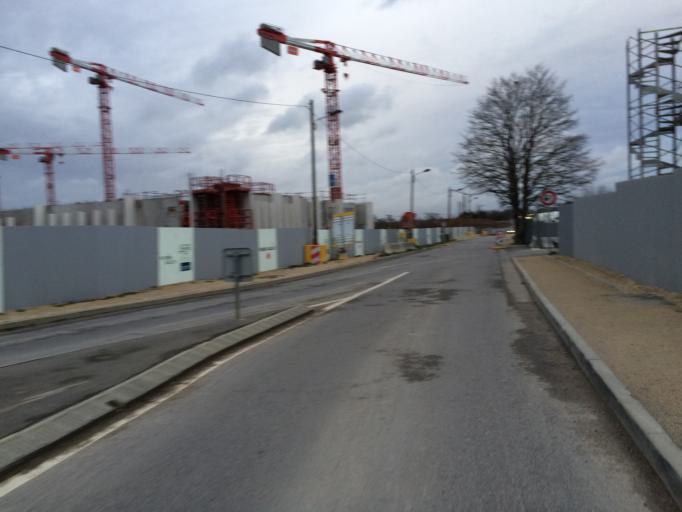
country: FR
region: Ile-de-France
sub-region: Departement de l'Essonne
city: Bures-sur-Yvette
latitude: 48.7107
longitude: 2.1765
